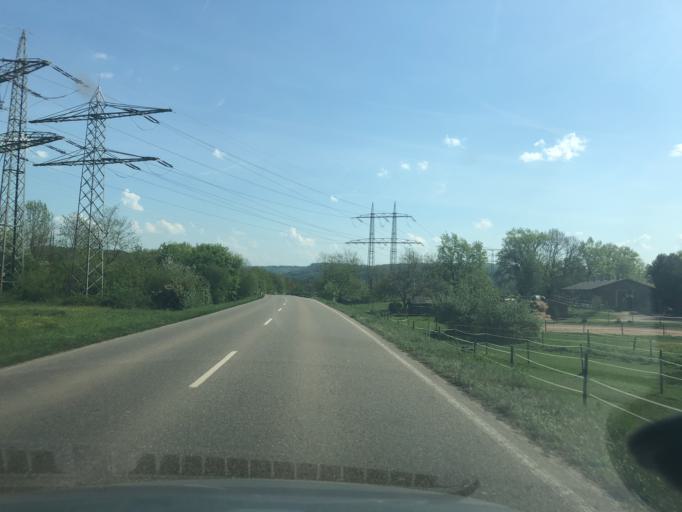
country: CH
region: Aargau
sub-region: Bezirk Zurzach
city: Koblenz
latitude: 47.6306
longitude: 8.2530
